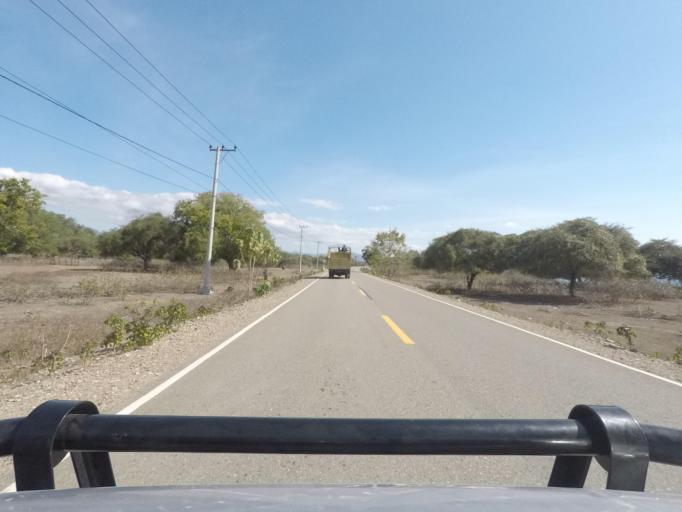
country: ID
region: East Nusa Tenggara
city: Atambua
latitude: -8.9269
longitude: 124.9861
